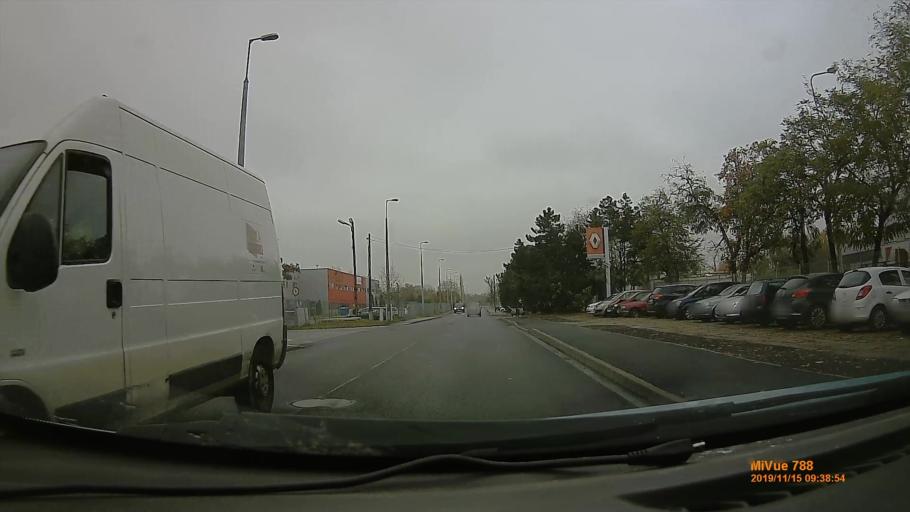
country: HU
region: Budapest
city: Budapest XX. keruelet
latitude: 47.4563
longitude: 19.1038
